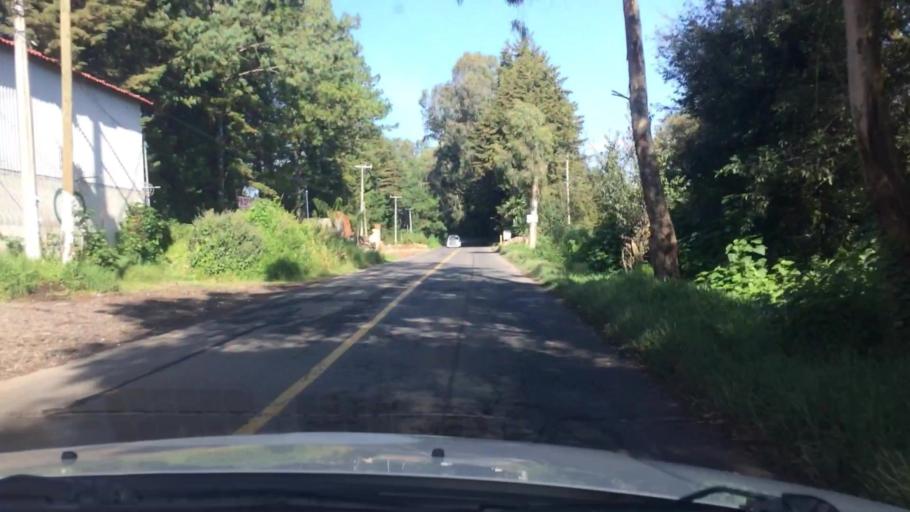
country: MX
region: Mexico
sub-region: Valle de Bravo
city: Cuadrilla de Dolores
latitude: 19.1468
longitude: -100.0639
